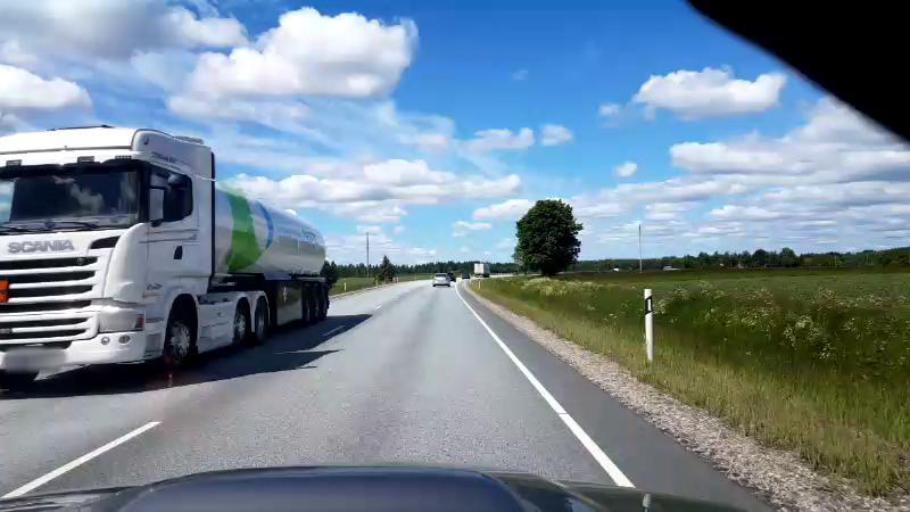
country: EE
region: Paernumaa
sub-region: Halinga vald
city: Parnu-Jaagupi
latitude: 58.5653
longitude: 24.5149
